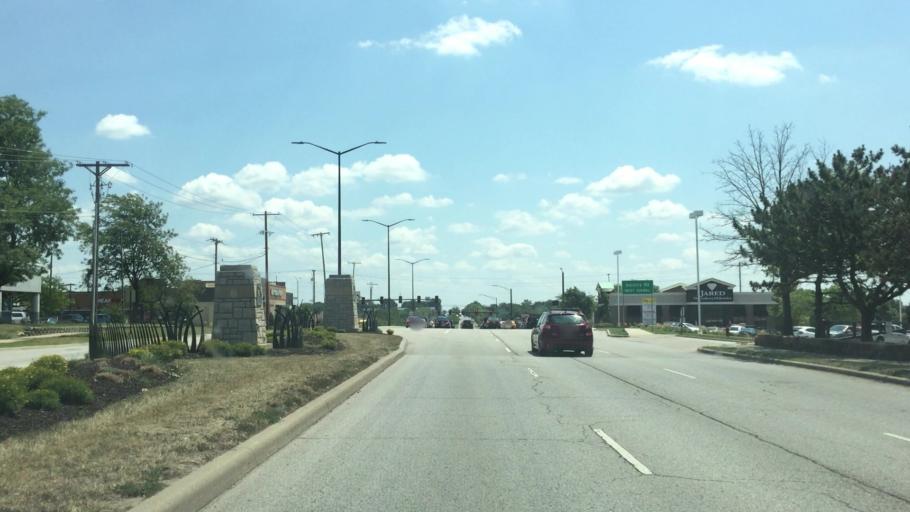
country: US
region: Kansas
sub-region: Johnson County
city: Lenexa
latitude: 38.9565
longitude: -94.7258
